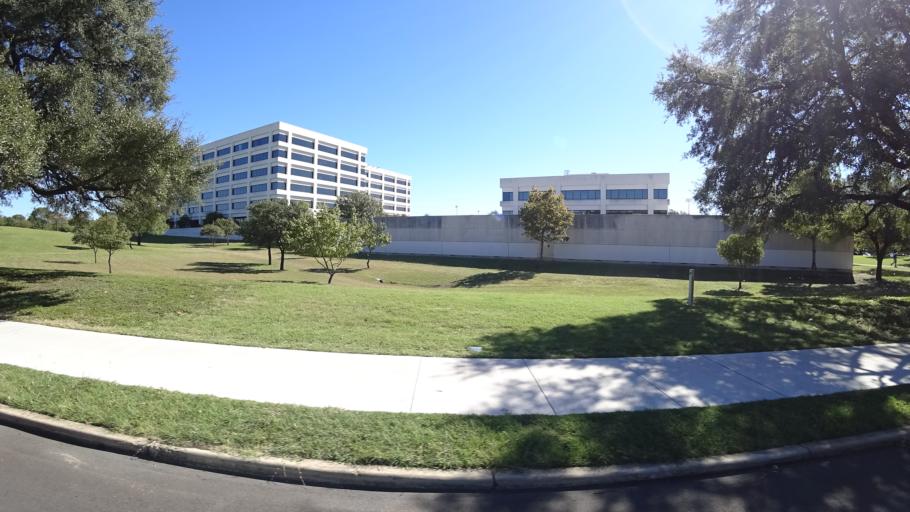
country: US
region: Texas
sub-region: Travis County
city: Austin
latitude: 30.3156
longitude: -97.7322
